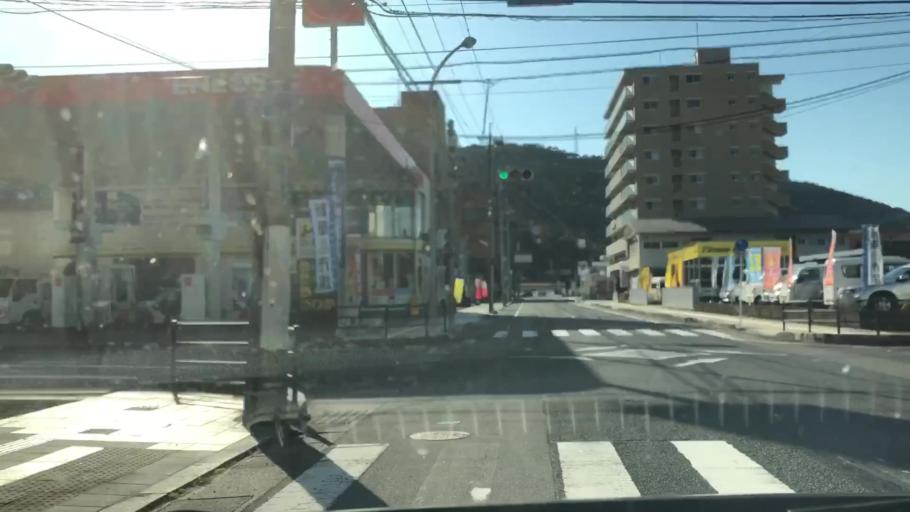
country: JP
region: Kagoshima
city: Satsumasendai
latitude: 31.8157
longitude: 130.3027
